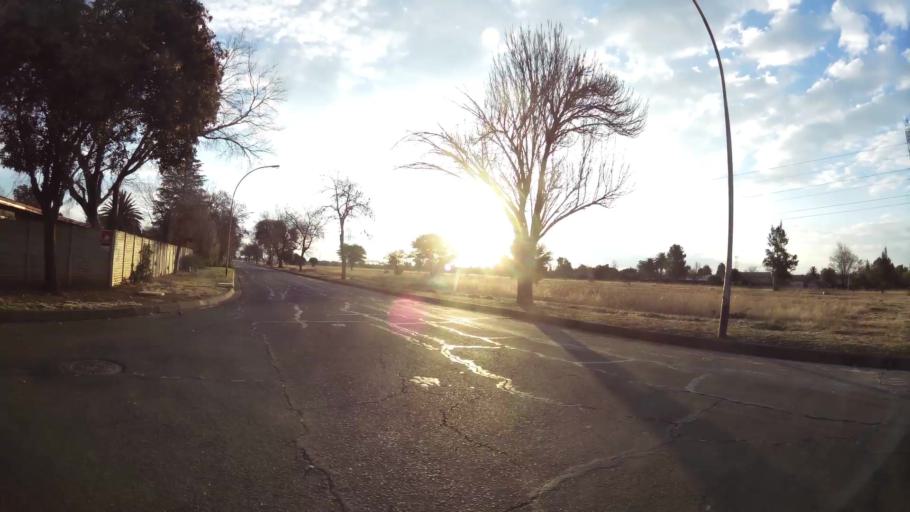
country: ZA
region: Orange Free State
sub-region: Mangaung Metropolitan Municipality
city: Bloemfontein
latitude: -29.1343
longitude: 26.1799
